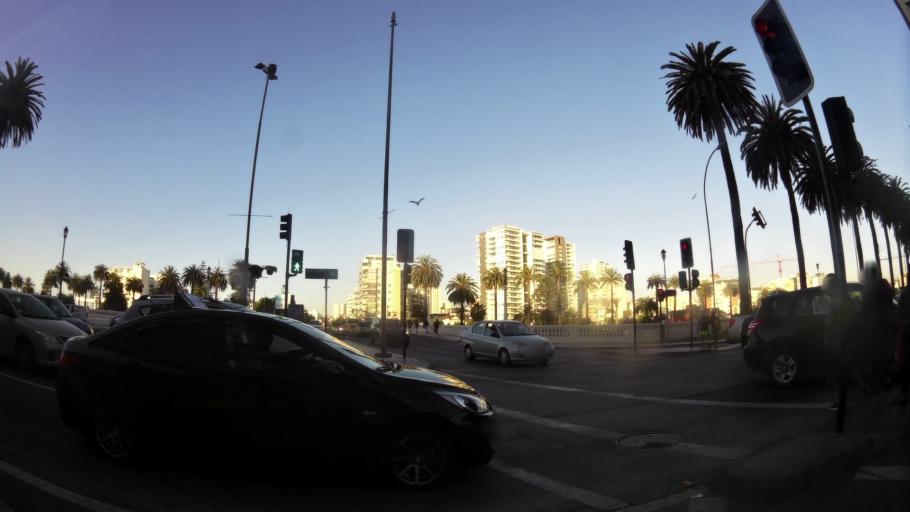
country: CL
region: Valparaiso
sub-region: Provincia de Valparaiso
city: Vina del Mar
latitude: -33.0215
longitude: -71.5609
